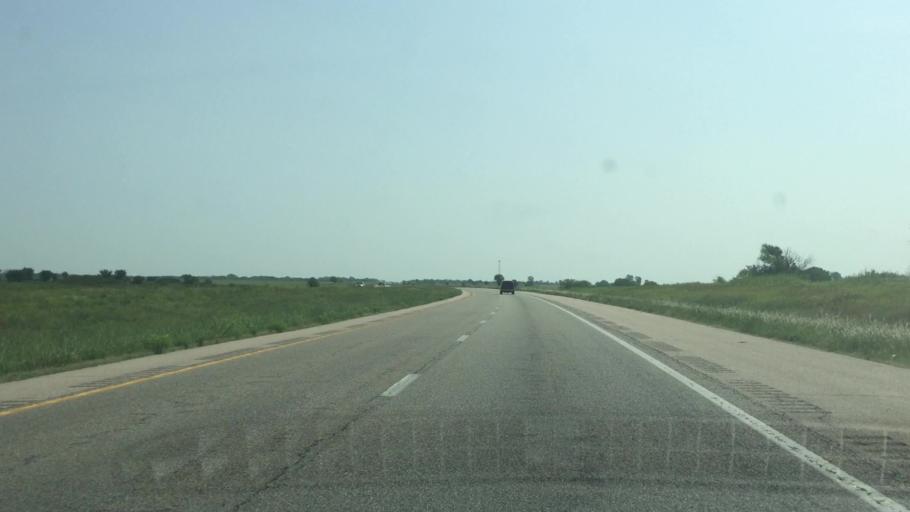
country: US
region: Kansas
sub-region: Osage County
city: Osage City
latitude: 38.4142
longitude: -95.9301
